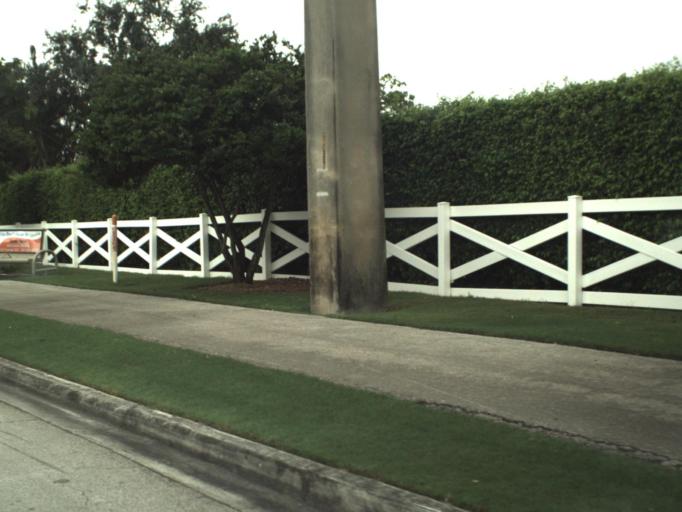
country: US
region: Florida
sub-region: Palm Beach County
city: Kings Point
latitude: 26.4212
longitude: -80.1220
